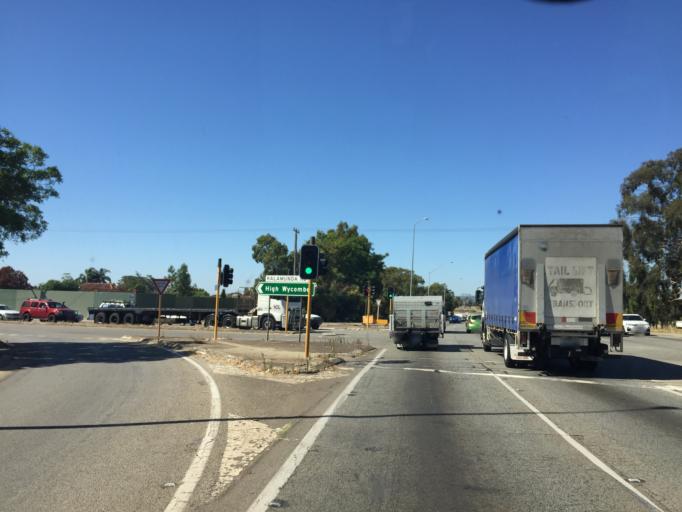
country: AU
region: Western Australia
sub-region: Kalamunda
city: Maida Vale
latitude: -31.9409
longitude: 116.0158
